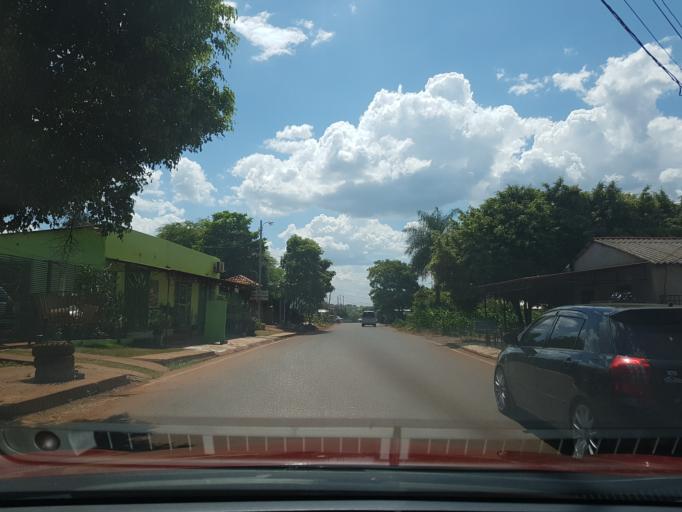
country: PY
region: Alto Parana
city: Ciudad del Este
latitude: -25.4825
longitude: -54.6794
